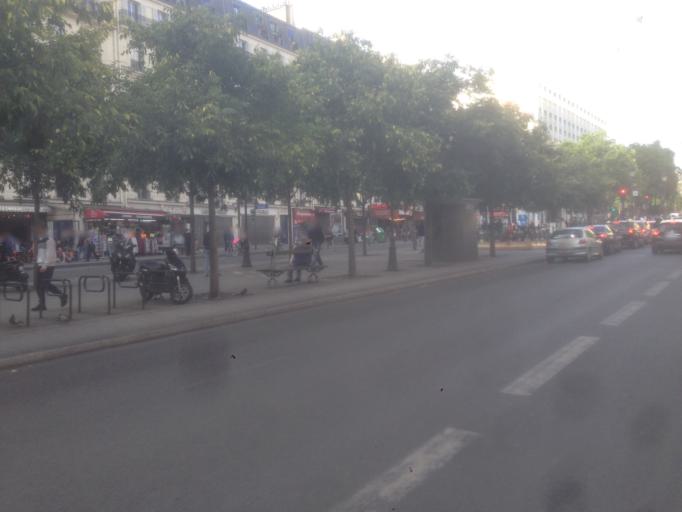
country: FR
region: Ile-de-France
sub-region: Paris
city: Saint-Ouen
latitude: 48.8840
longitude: 2.3288
